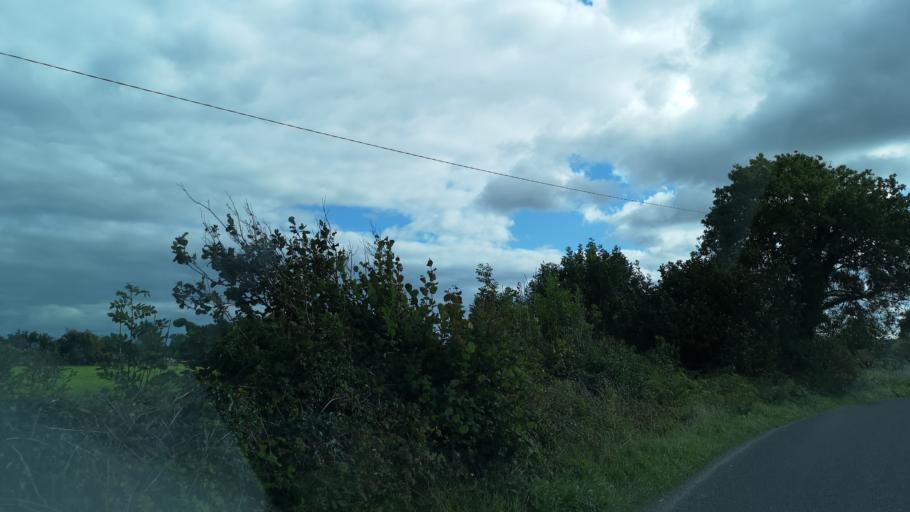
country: IE
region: Connaught
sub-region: County Galway
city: Moycullen
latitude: 53.3540
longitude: -9.1749
